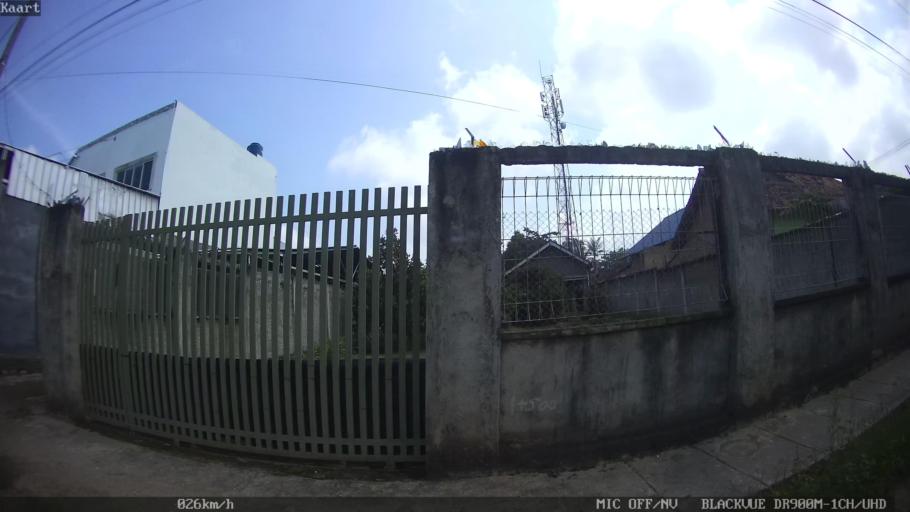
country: ID
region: Lampung
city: Kedaton
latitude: -5.3406
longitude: 105.2806
